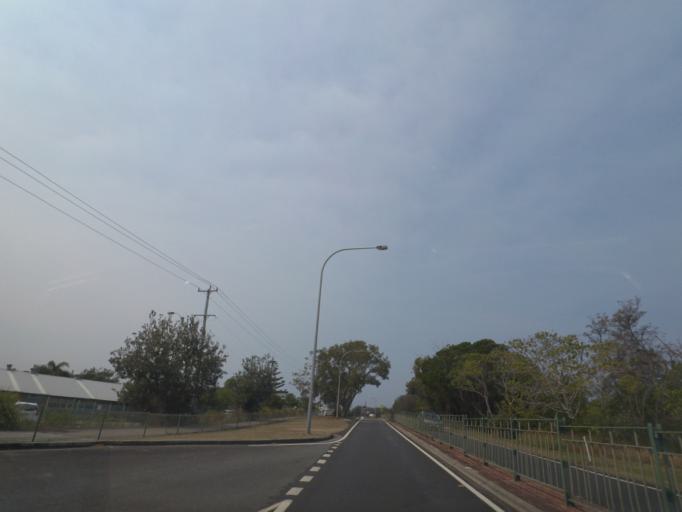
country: AU
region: New South Wales
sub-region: Tweed
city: Casuarina
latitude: -28.3383
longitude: 153.5732
